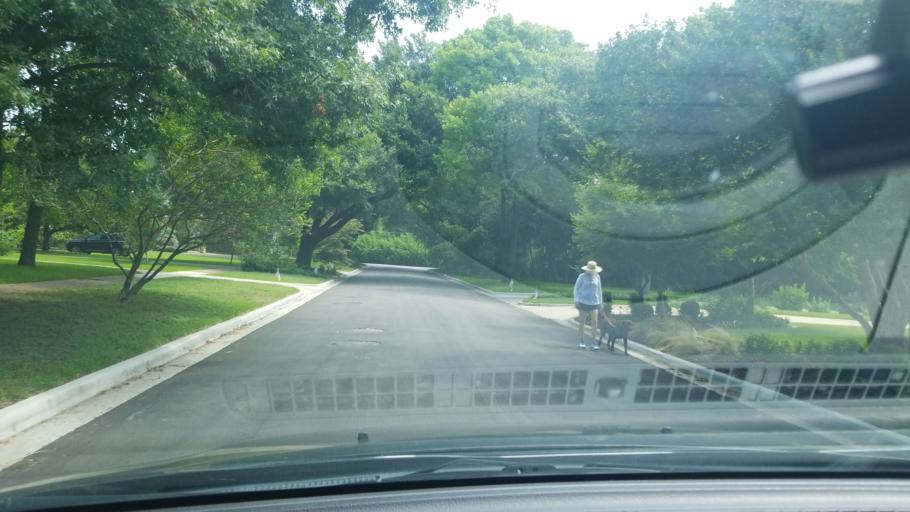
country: US
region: Texas
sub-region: Dallas County
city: Highland Park
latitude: 32.8211
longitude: -96.7141
